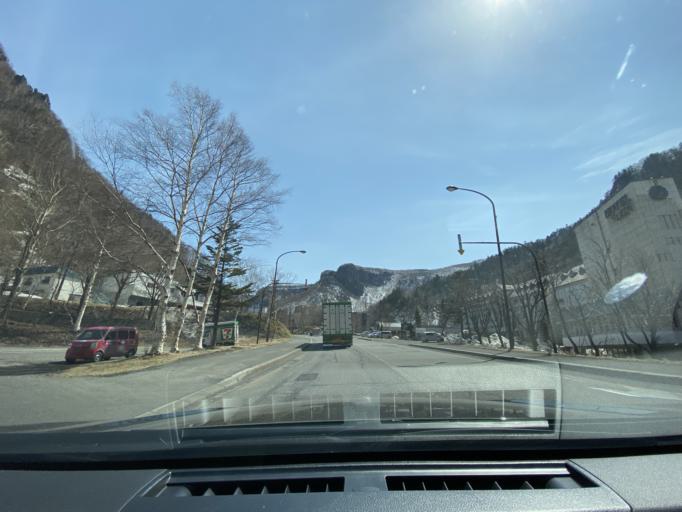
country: JP
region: Hokkaido
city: Kamikawa
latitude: 43.7305
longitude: 142.9425
